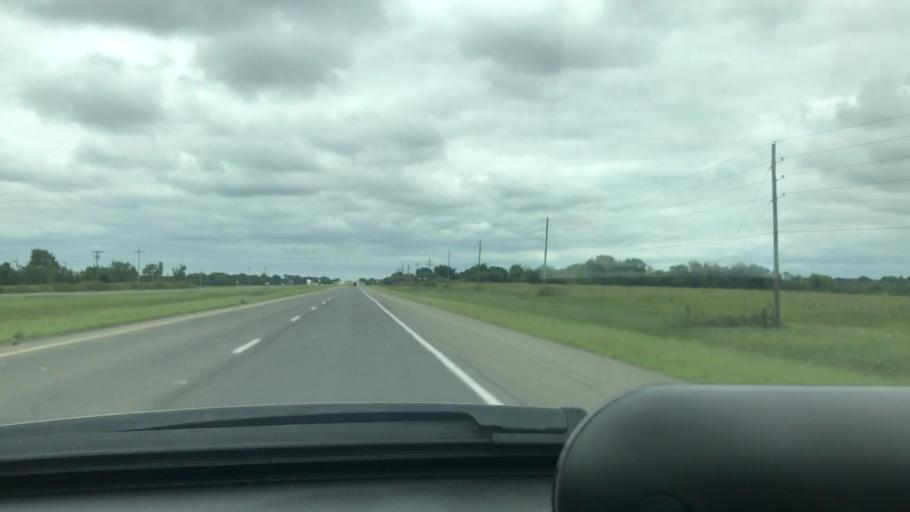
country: US
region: Oklahoma
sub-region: Wagoner County
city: Wagoner
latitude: 35.8612
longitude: -95.4026
